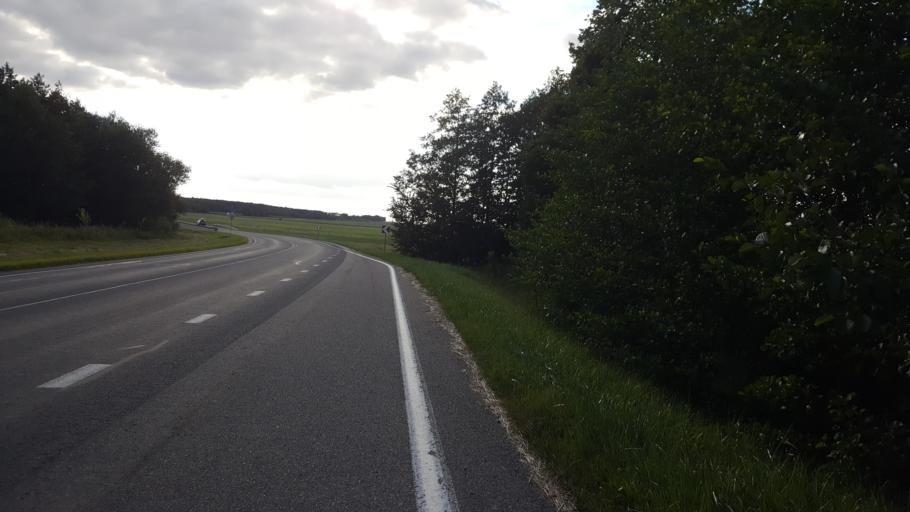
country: BY
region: Brest
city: Kamyanyets
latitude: 52.4007
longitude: 23.8988
